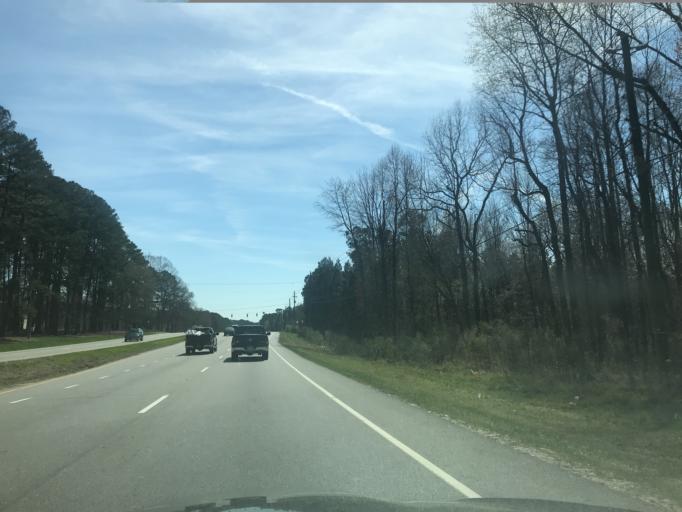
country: US
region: North Carolina
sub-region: Wake County
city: Garner
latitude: 35.6527
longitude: -78.7066
